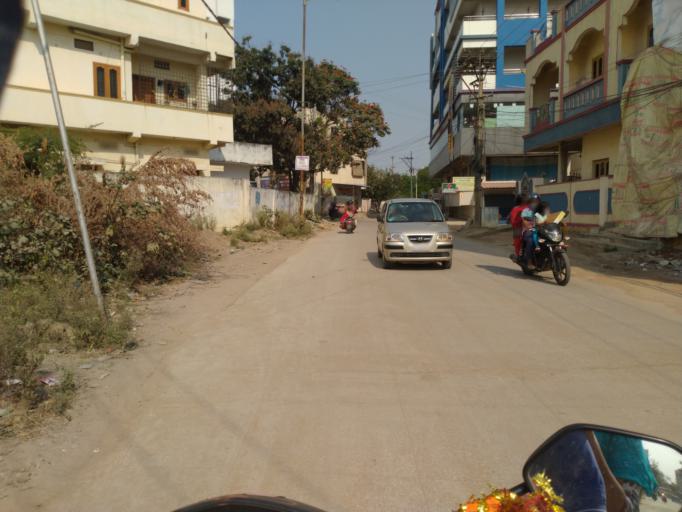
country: IN
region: Telangana
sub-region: Rangareddi
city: Quthbullapur
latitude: 17.4967
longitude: 78.4673
